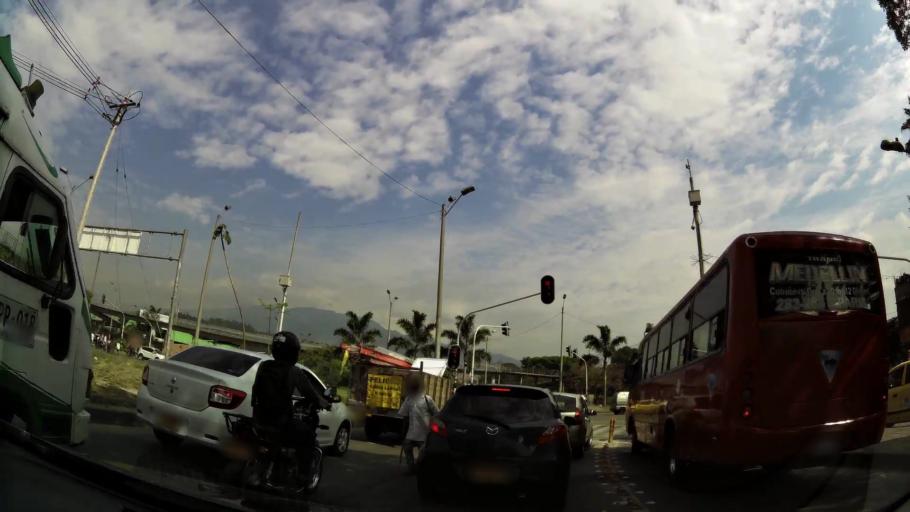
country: CO
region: Antioquia
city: Medellin
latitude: 6.2567
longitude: -75.5718
